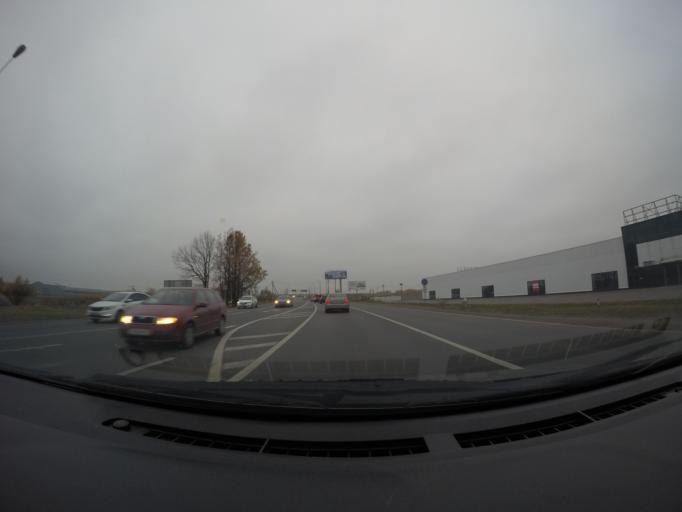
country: RU
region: Moskovskaya
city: Bronnitsy
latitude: 55.4156
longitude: 38.2451
